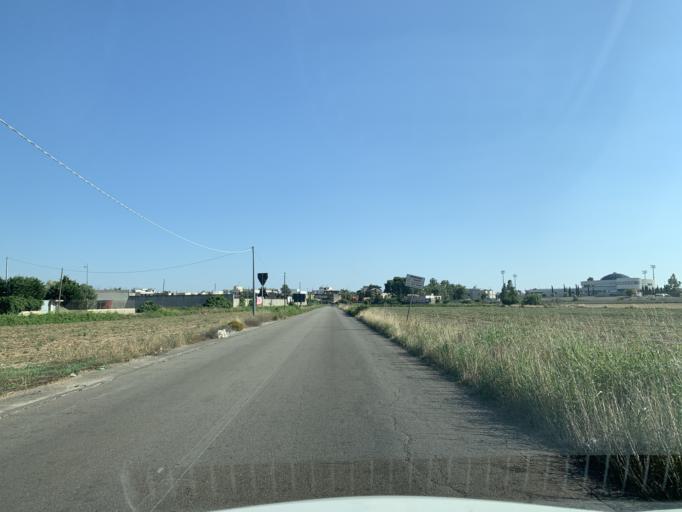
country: IT
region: Apulia
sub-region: Provincia di Lecce
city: Nardo
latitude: 40.1881
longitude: 18.0392
